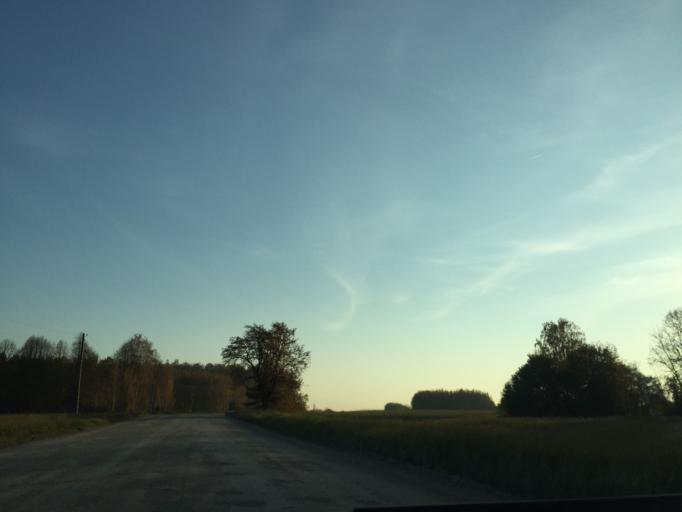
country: LV
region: Vainode
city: Vainode
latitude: 56.5406
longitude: 21.8365
